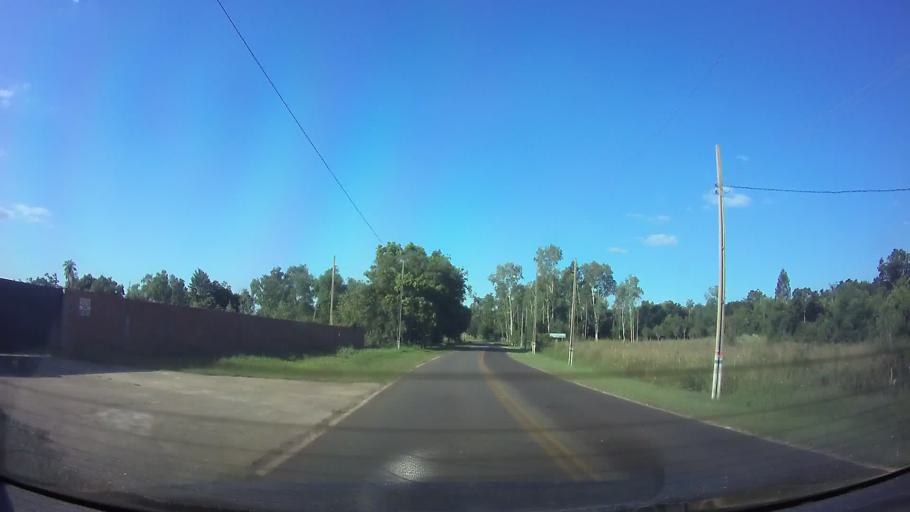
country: PY
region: Cordillera
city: Atyra
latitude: -25.3030
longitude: -57.1863
